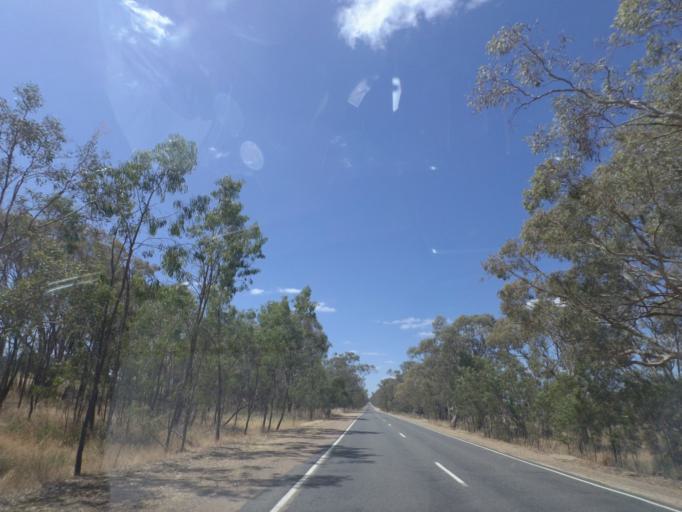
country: AU
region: Victoria
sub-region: Wangaratta
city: Wangaratta
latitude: -36.4412
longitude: 146.2454
